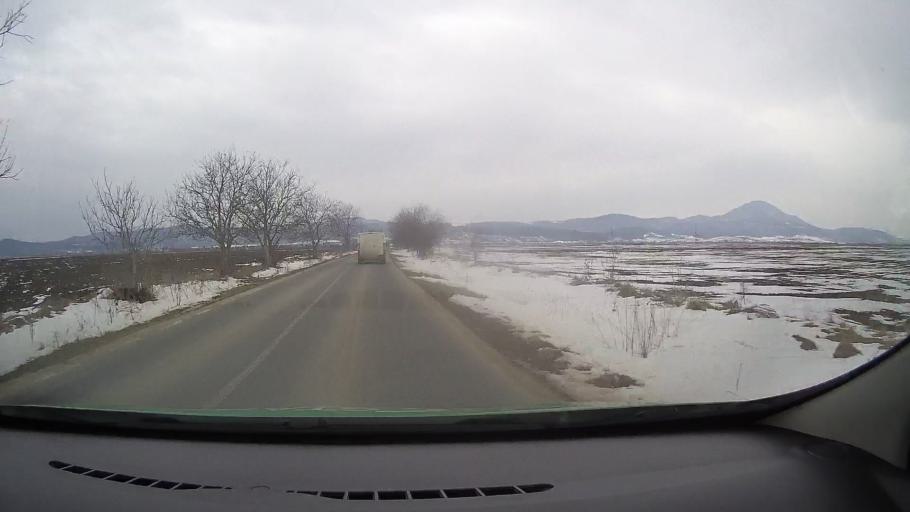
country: RO
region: Brasov
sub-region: Comuna Cristian
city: Cristian
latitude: 45.6348
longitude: 25.4506
